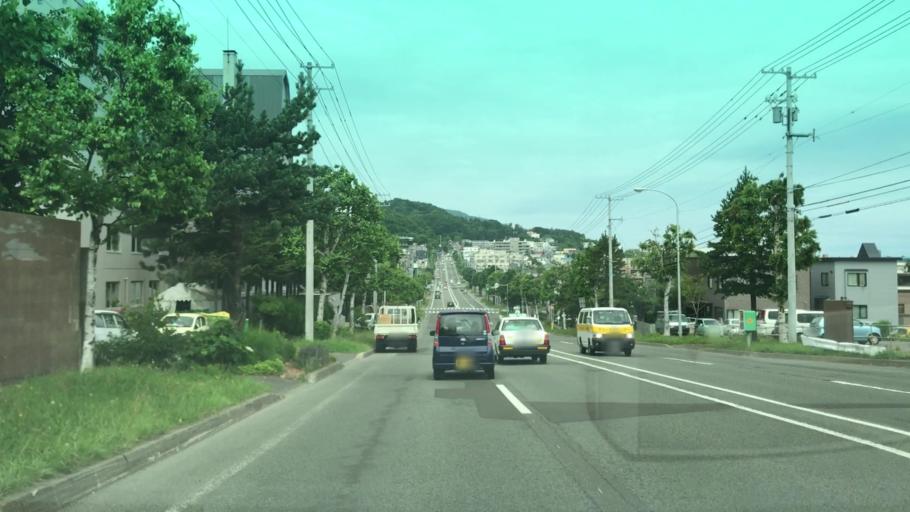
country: JP
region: Hokkaido
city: Sapporo
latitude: 43.0598
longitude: 141.2982
